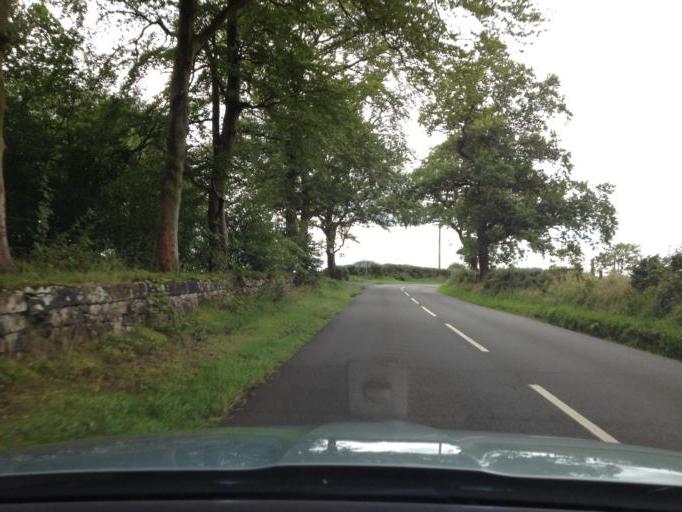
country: GB
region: Scotland
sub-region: Falkirk
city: Falkirk
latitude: 55.9892
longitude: -3.8161
